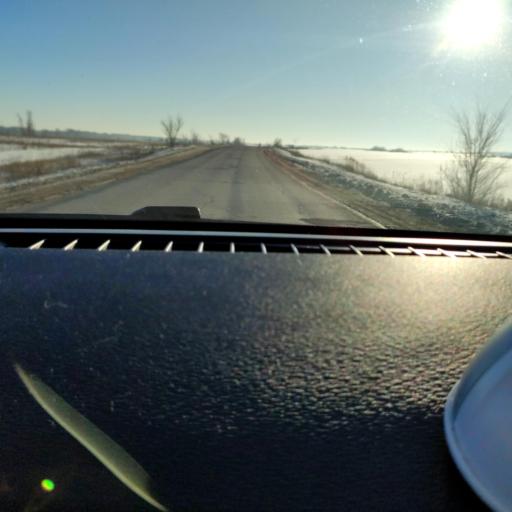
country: RU
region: Samara
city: Spiridonovka
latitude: 53.1330
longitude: 50.6113
